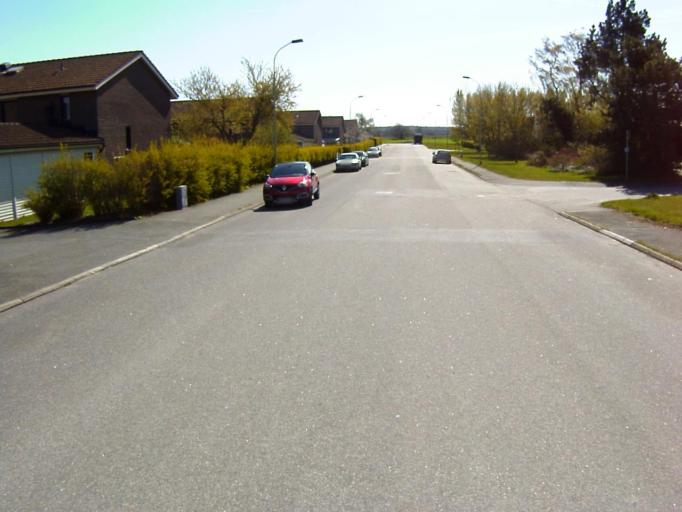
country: SE
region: Skane
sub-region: Kristianstads Kommun
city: Norra Asum
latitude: 55.9989
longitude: 14.0900
